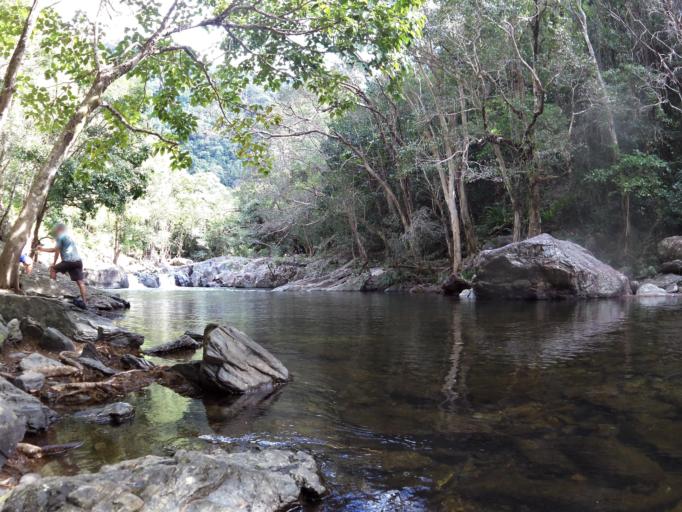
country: AU
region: Queensland
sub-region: Cairns
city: Woree
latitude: -16.9645
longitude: 145.6772
